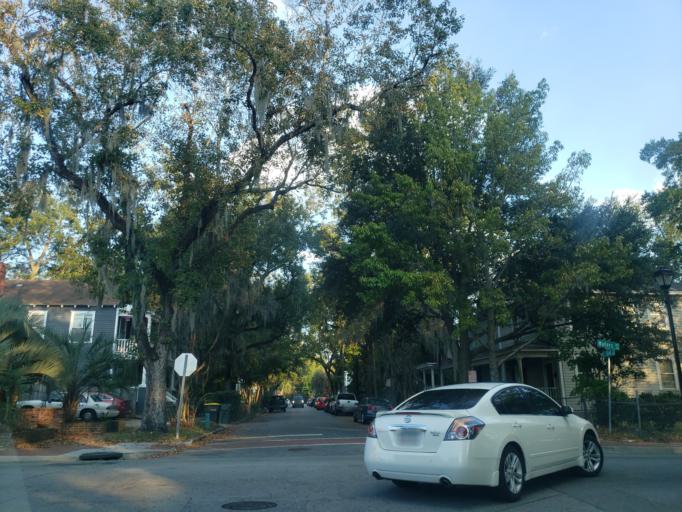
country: US
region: Georgia
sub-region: Chatham County
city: Savannah
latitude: 32.0559
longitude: -81.0827
